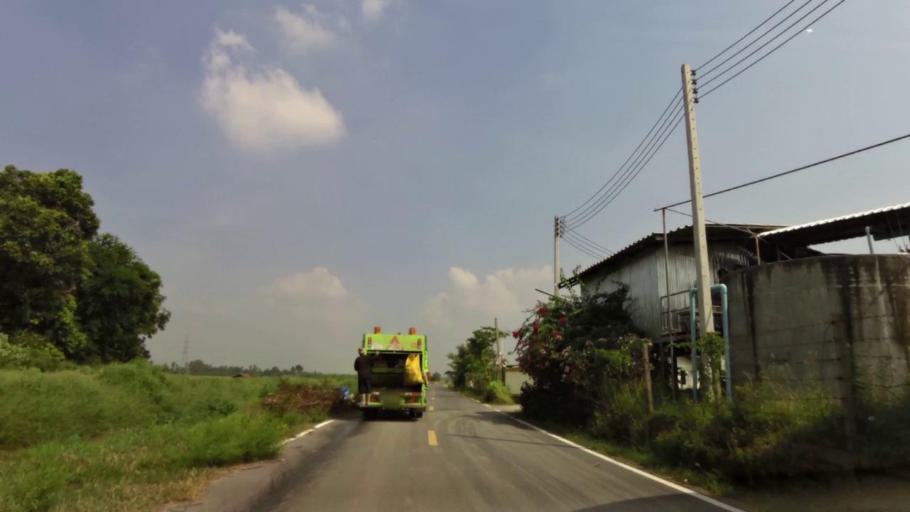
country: TH
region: Ang Thong
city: Pho Thong
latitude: 14.6125
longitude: 100.3984
